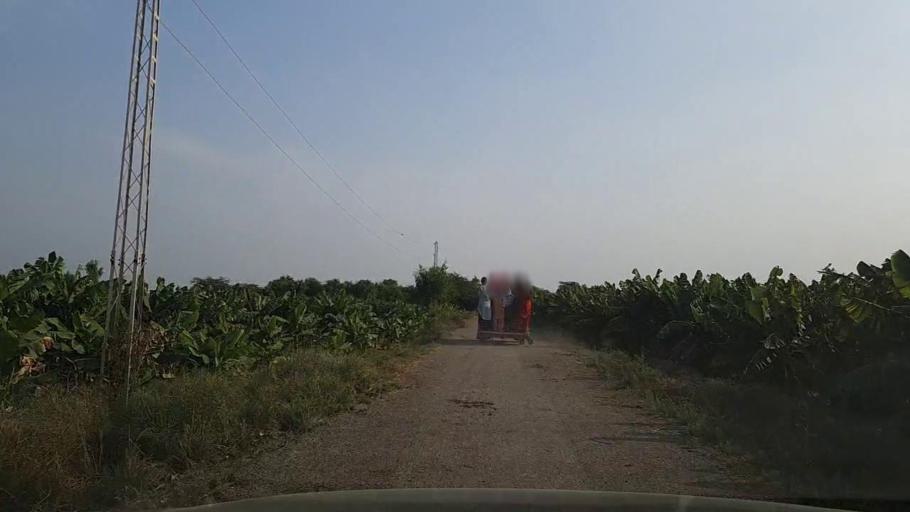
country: PK
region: Sindh
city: Thatta
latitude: 24.6415
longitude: 67.9510
